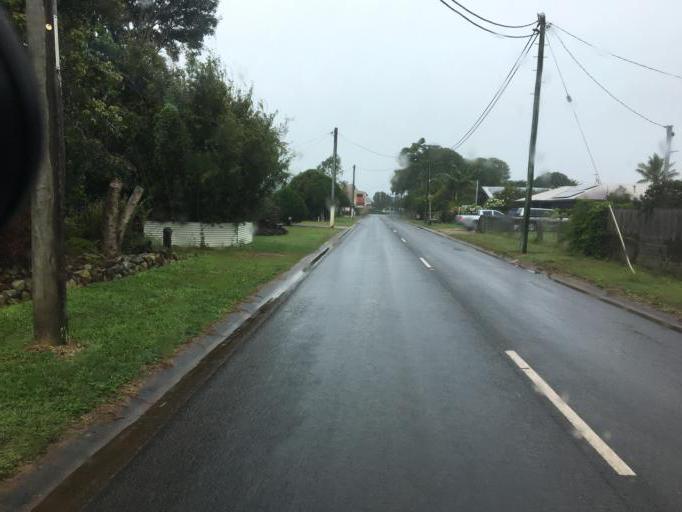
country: AU
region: Queensland
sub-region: Tablelands
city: Tolga
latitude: -17.2158
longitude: 145.5410
